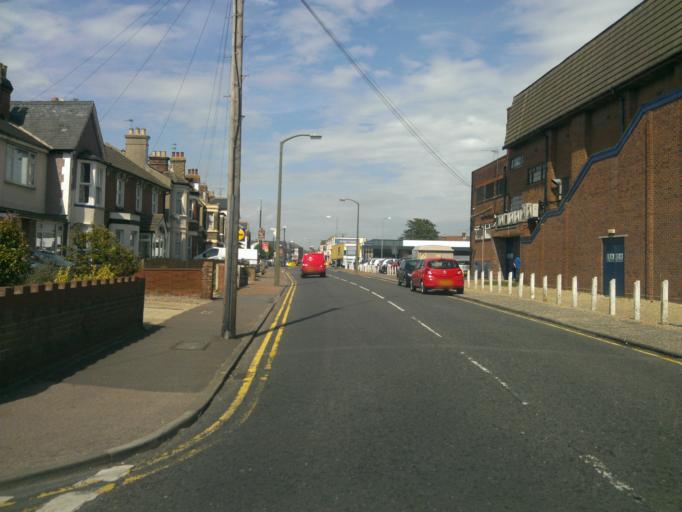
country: GB
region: England
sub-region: Essex
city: Clacton-on-Sea
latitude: 51.7915
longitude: 1.1482
